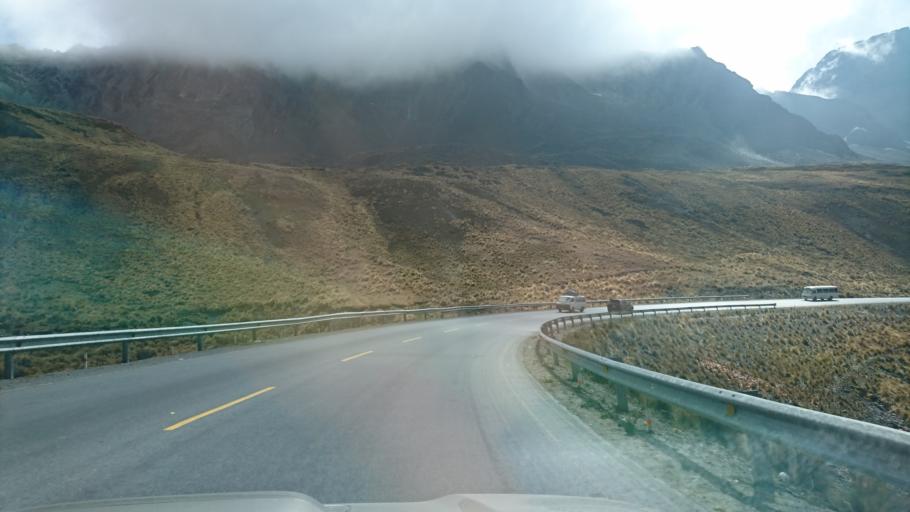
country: BO
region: La Paz
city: La Paz
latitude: -16.3176
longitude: -68.0362
